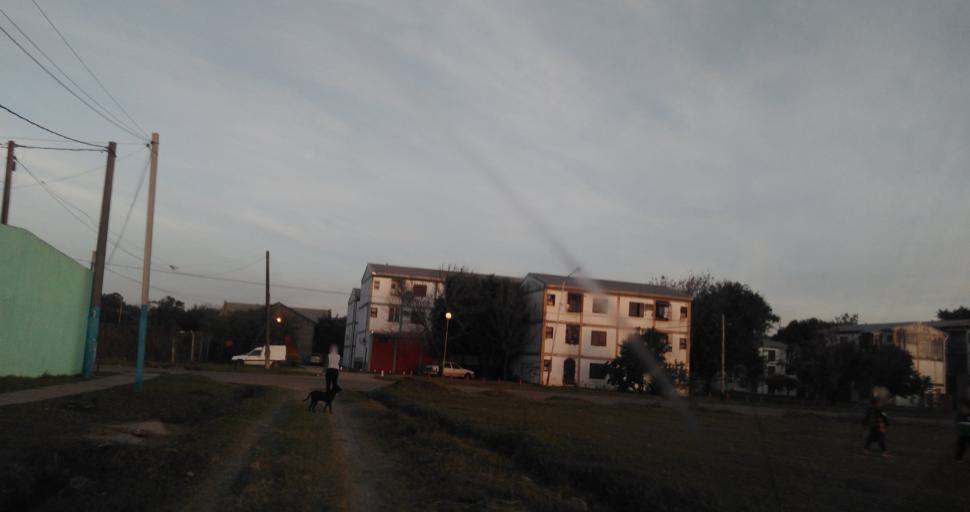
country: AR
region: Chaco
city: Resistencia
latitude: -27.4662
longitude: -59.0109
